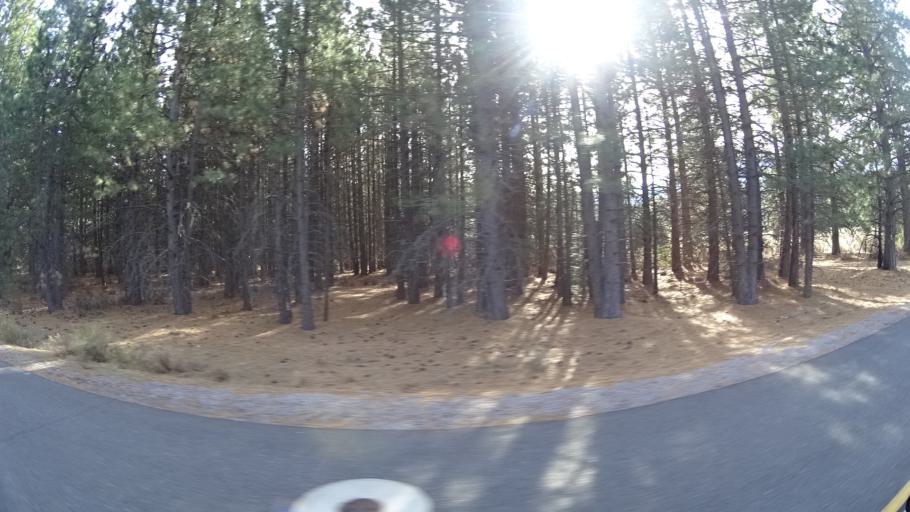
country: US
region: California
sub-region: Siskiyou County
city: Weed
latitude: 41.3945
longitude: -122.3869
